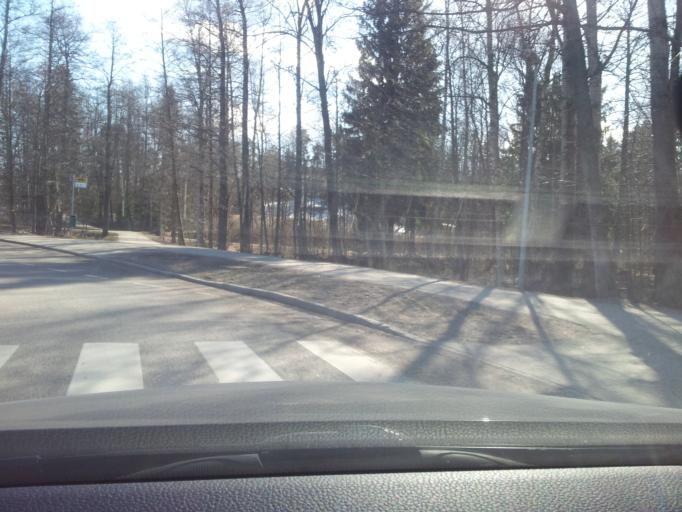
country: FI
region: Uusimaa
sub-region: Helsinki
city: Koukkuniemi
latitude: 60.1652
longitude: 24.7890
